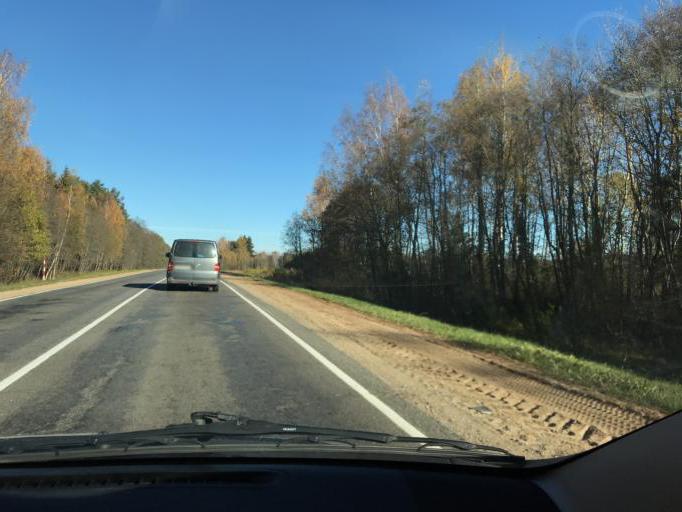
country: BY
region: Vitebsk
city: Polatsk
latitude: 55.3238
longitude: 28.7820
